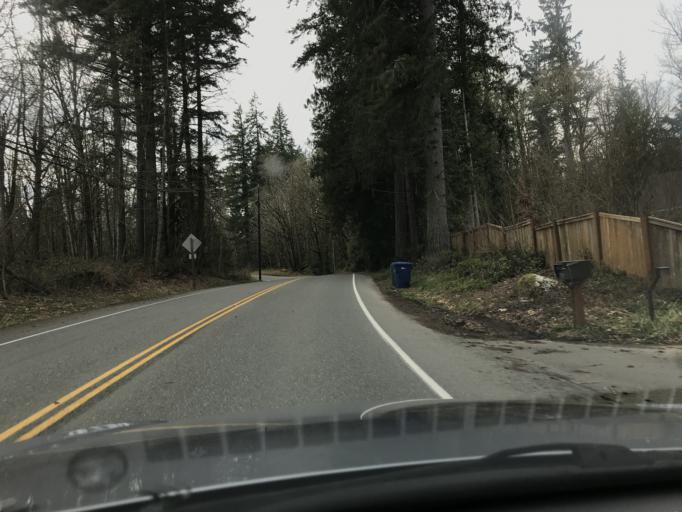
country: US
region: Washington
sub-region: King County
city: Union Hill-Novelty Hill
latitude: 47.6615
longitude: -122.0111
